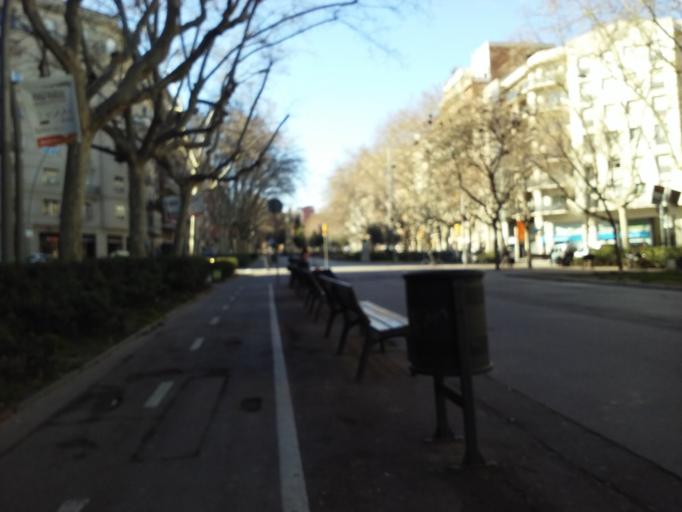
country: ES
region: Catalonia
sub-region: Provincia de Barcelona
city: Gracia
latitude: 41.4023
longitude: 2.1658
